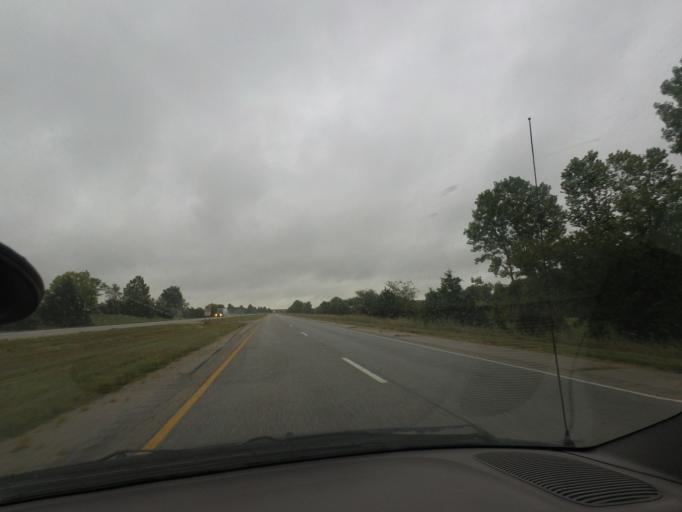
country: US
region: Illinois
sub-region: Pike County
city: Barry
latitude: 39.7361
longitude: -91.1476
